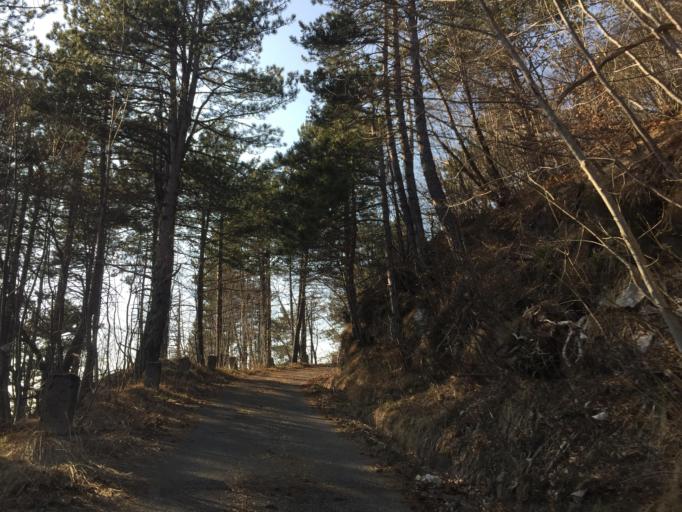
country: IT
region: Friuli Venezia Giulia
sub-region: Provincia di Udine
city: Amaro
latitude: 46.3877
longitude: 13.0716
